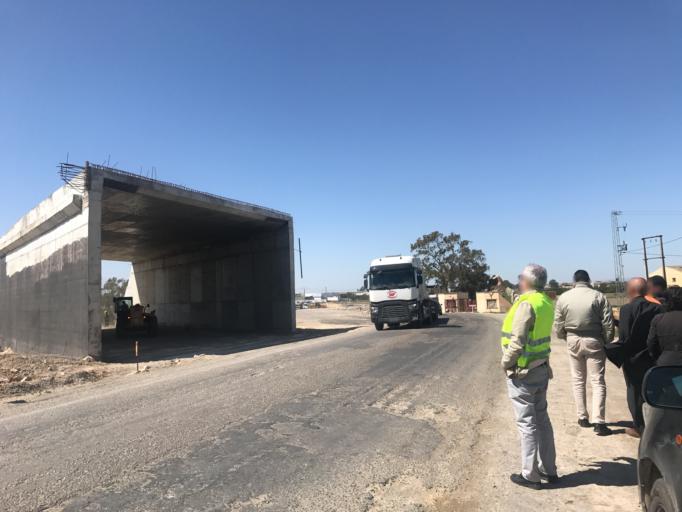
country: TN
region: Susah
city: Sidi el Hani
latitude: 35.6823
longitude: 10.3300
